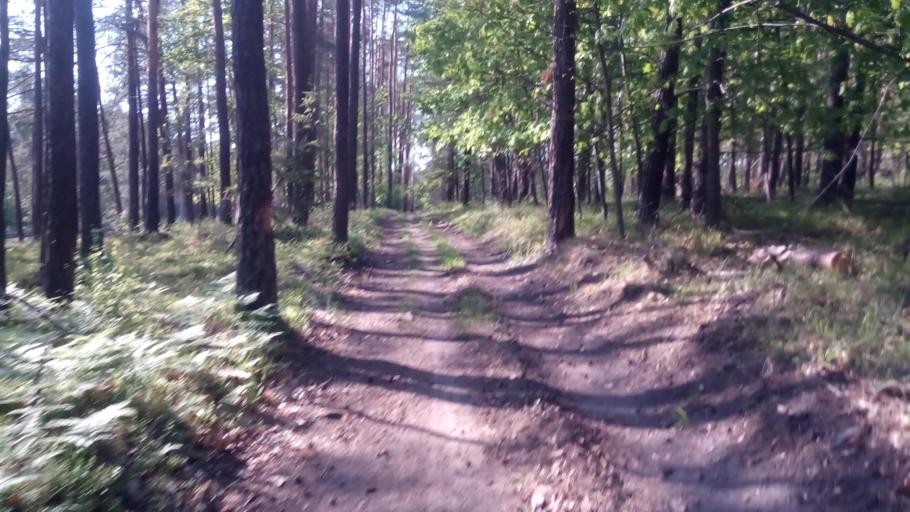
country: PL
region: Opole Voivodeship
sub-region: Powiat opolski
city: Tarnow Opolski
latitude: 50.5861
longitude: 18.0518
